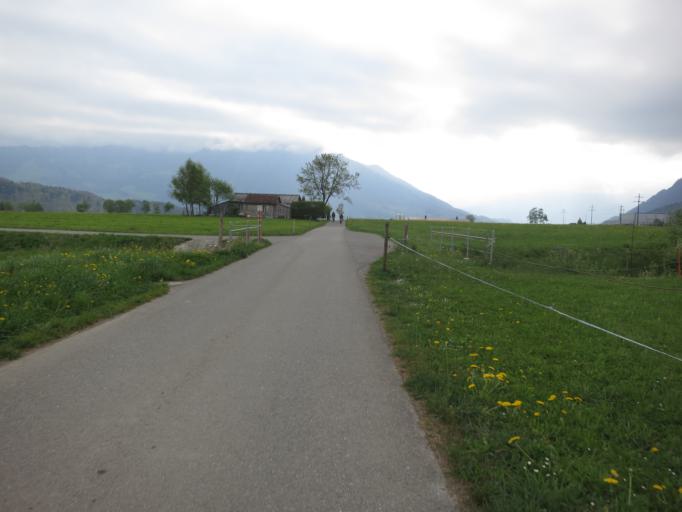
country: CH
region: Schwyz
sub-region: Bezirk March
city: Reichenburg
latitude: 47.1732
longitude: 8.9876
